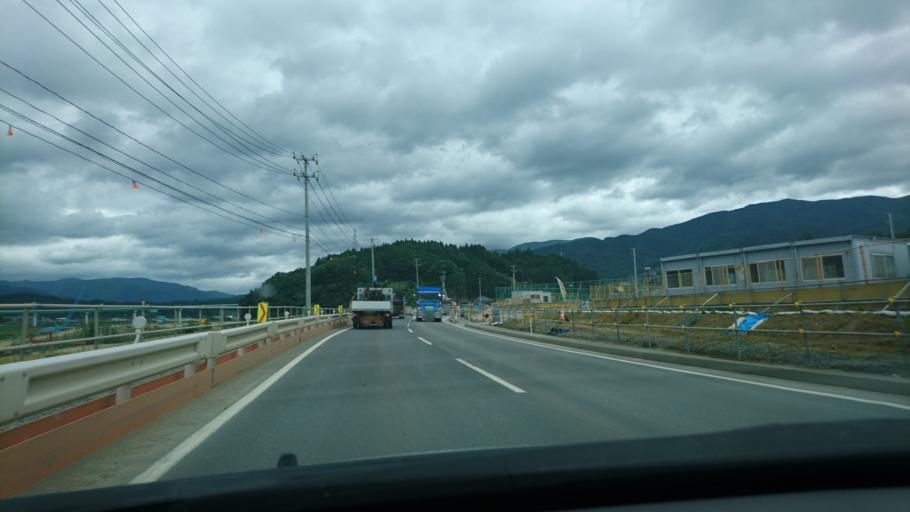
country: JP
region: Iwate
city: Ofunato
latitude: 39.0187
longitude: 141.6218
